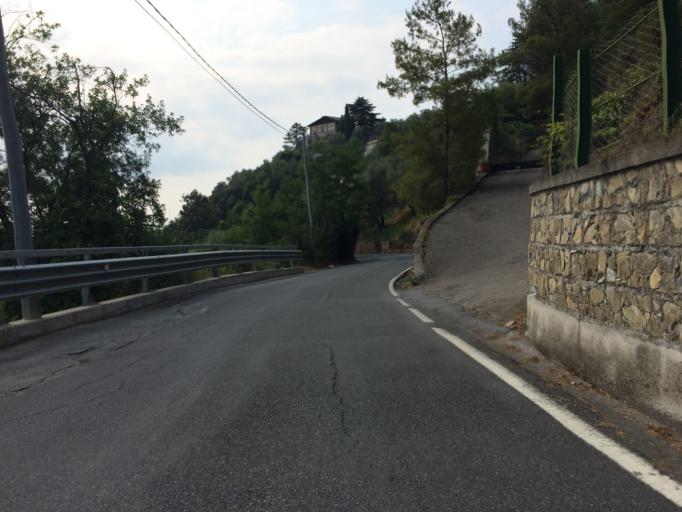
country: IT
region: Liguria
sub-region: Provincia di Imperia
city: San Remo
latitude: 43.8384
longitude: 7.7545
